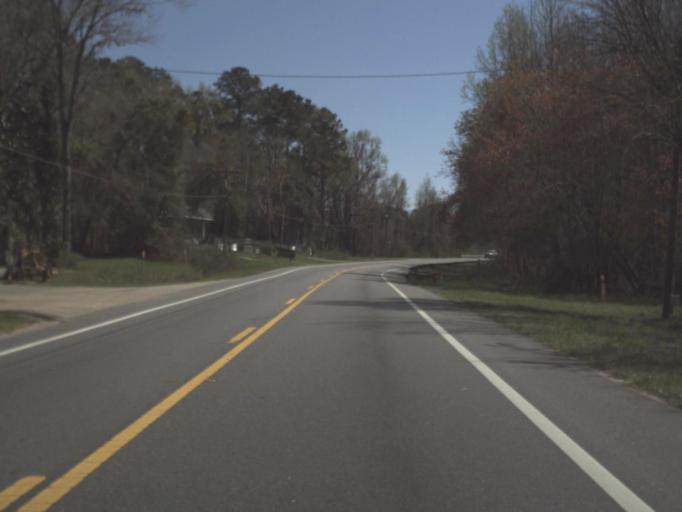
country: US
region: Florida
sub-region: Gadsden County
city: Midway
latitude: 30.5113
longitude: -84.3634
